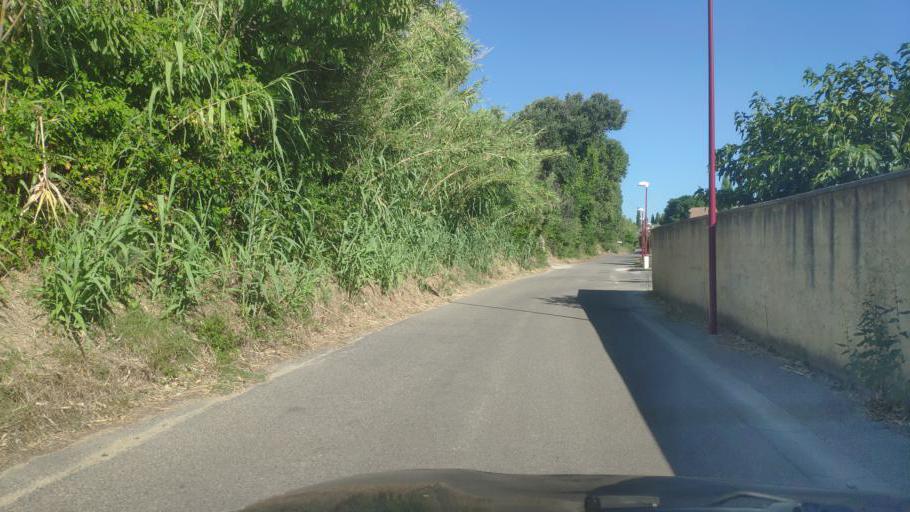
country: FR
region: Provence-Alpes-Cote d'Azur
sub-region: Departement du Vaucluse
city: Aubignan
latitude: 44.0945
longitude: 5.0316
